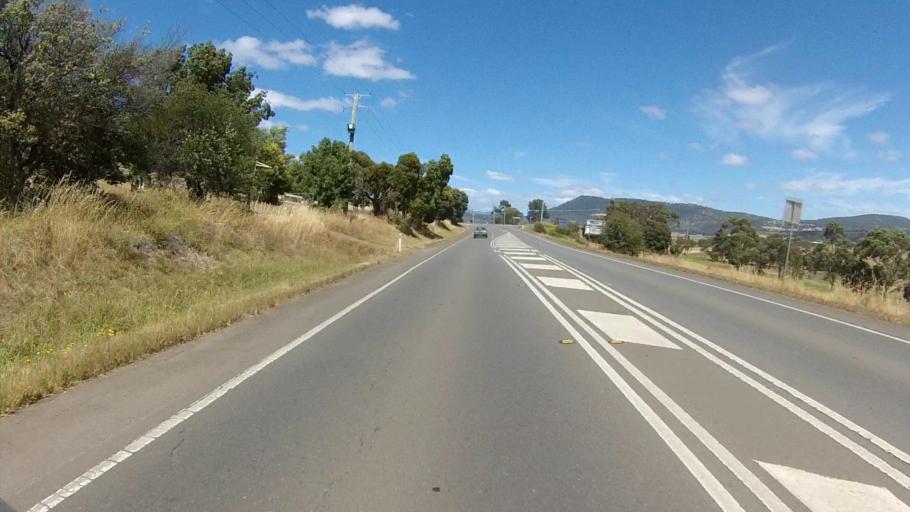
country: AU
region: Tasmania
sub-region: Clarence
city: Cambridge
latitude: -42.7418
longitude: 147.4216
